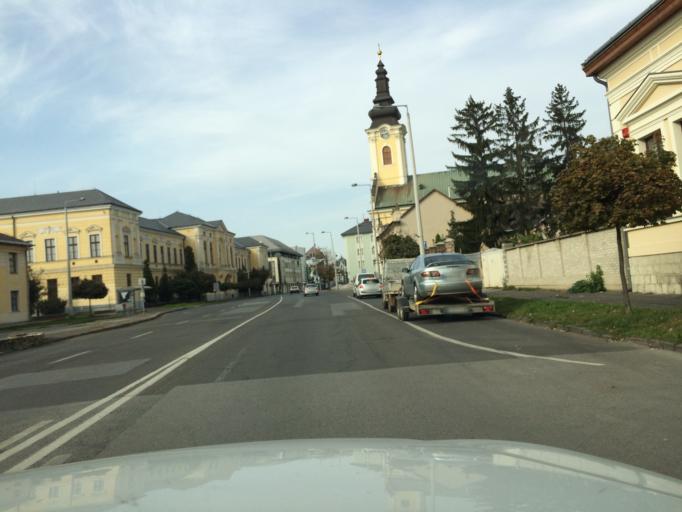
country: HU
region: Szabolcs-Szatmar-Bereg
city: Nyiregyhaza
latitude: 47.9518
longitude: 21.7189
